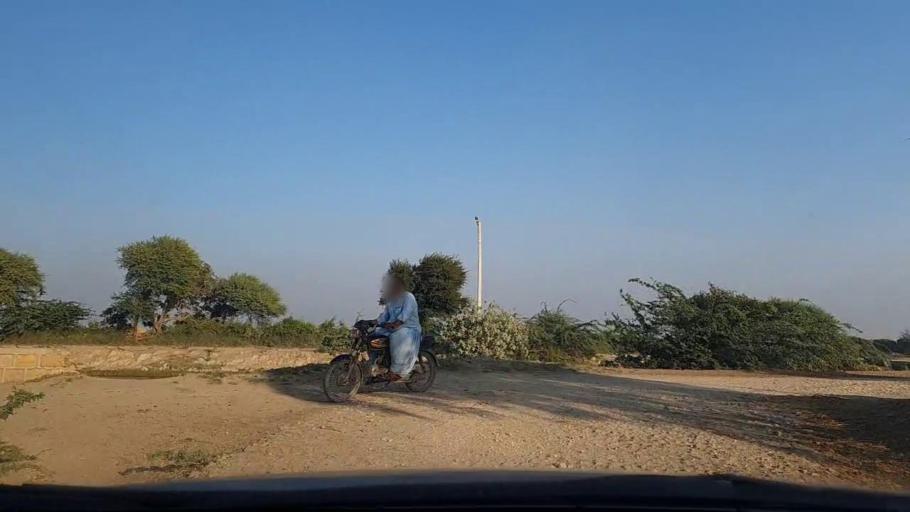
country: PK
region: Sindh
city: Mirpur Sakro
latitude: 24.5229
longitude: 67.6531
